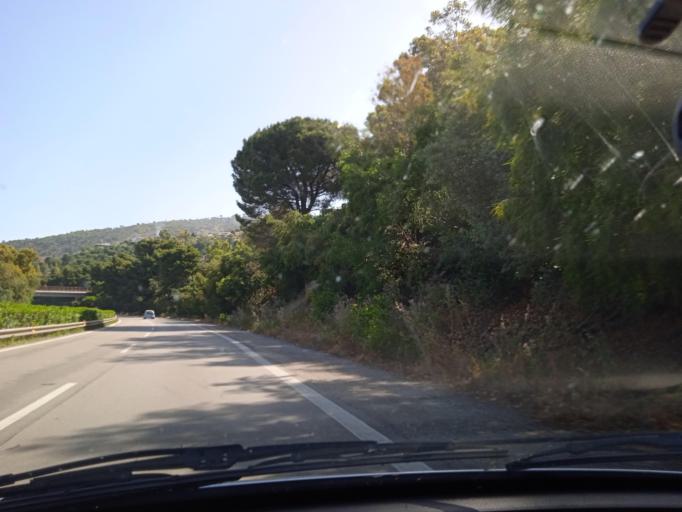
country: IT
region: Sicily
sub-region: Messina
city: Capo d'Orlando
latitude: 38.1305
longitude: 14.7350
